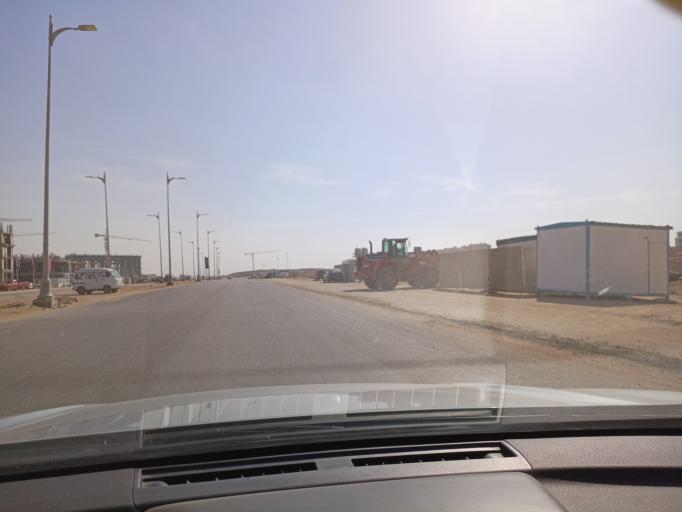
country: EG
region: Muhafazat al Qalyubiyah
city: Al Khankah
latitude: 30.0363
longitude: 31.6825
